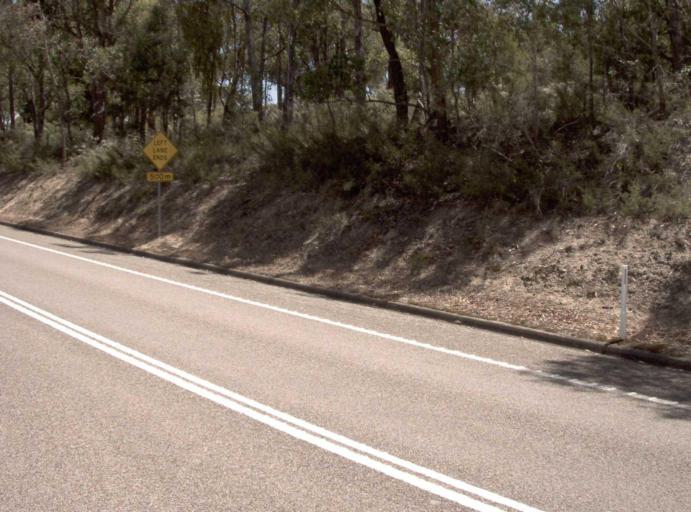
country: AU
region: Victoria
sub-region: East Gippsland
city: Bairnsdale
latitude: -37.7731
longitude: 147.6900
